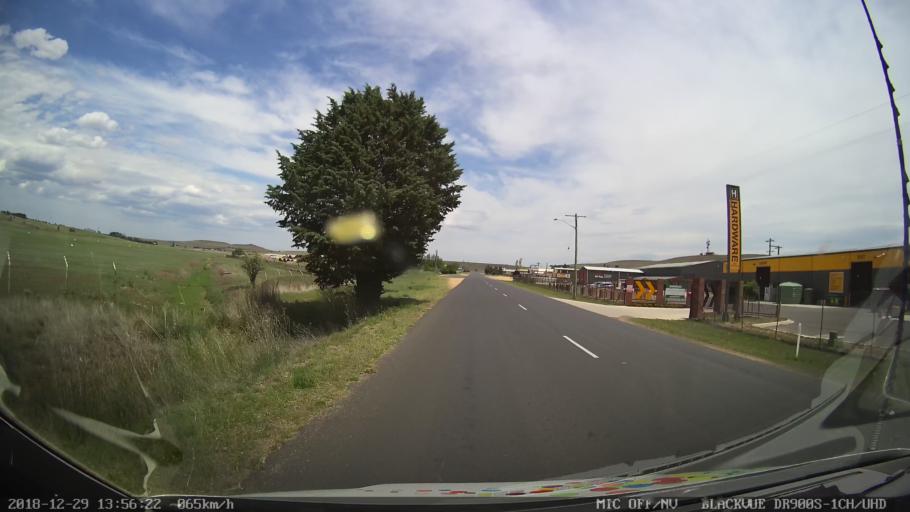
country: AU
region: New South Wales
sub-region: Cooma-Monaro
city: Cooma
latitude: -36.2299
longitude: 149.1463
